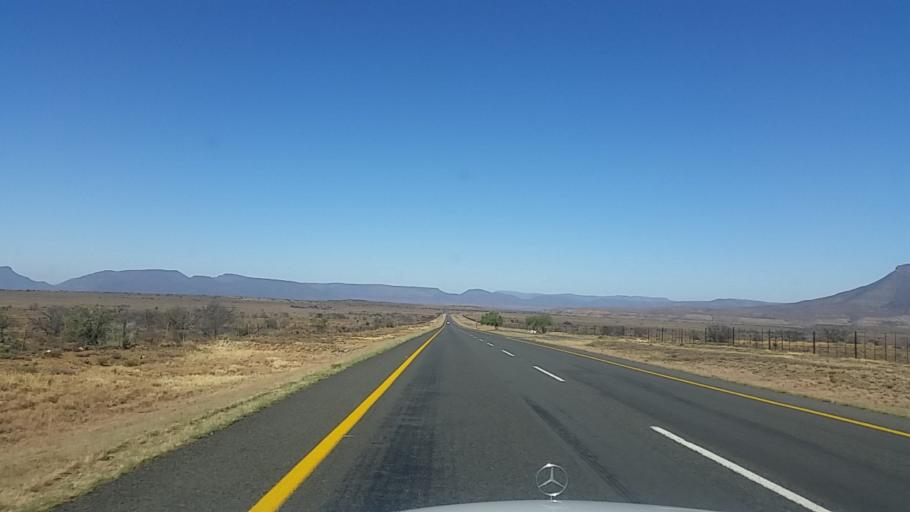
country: ZA
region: Eastern Cape
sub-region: Cacadu District Municipality
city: Graaff-Reinet
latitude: -32.1223
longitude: 24.6014
